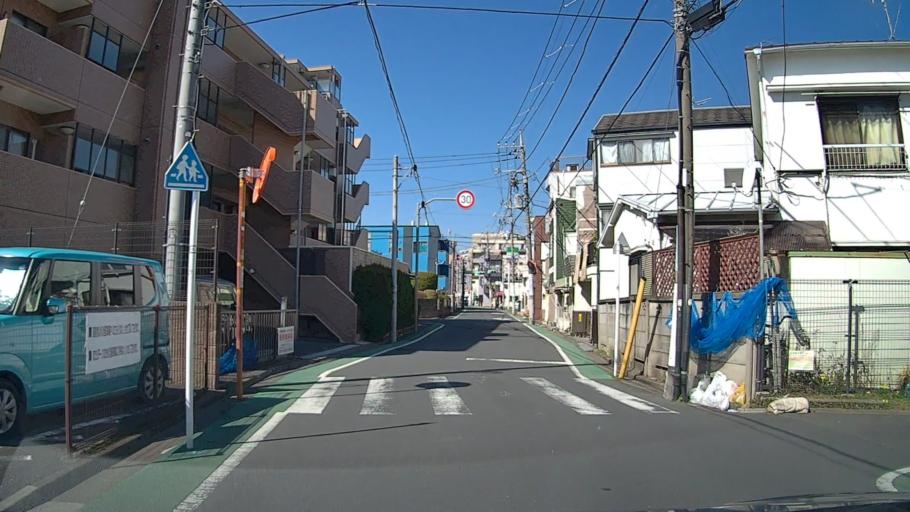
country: JP
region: Saitama
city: Wako
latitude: 35.7469
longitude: 139.5985
